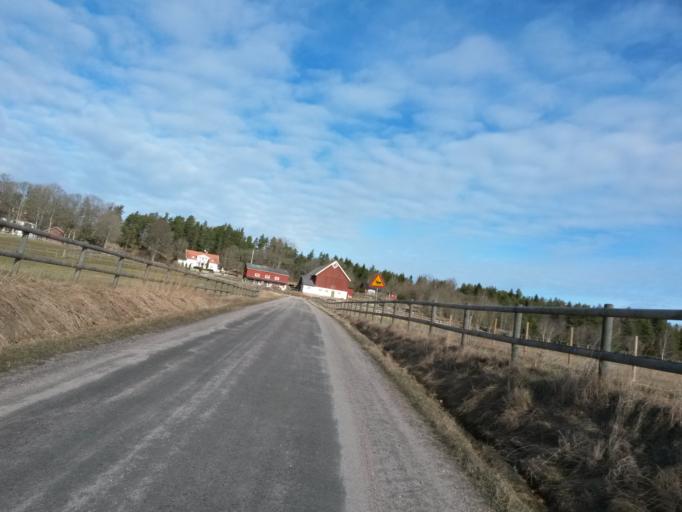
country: SE
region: Vaestra Goetaland
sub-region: Vargarda Kommun
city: Jonstorp
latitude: 57.9947
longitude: 12.6508
